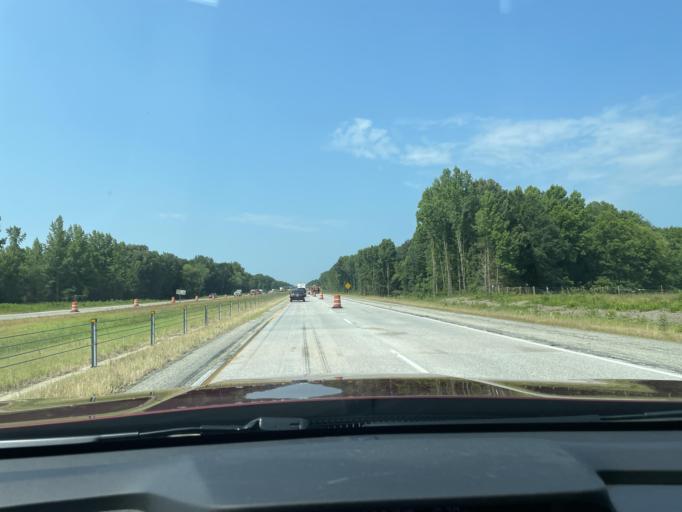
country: US
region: Arkansas
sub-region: White County
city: Searcy
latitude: 35.1805
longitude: -91.7590
